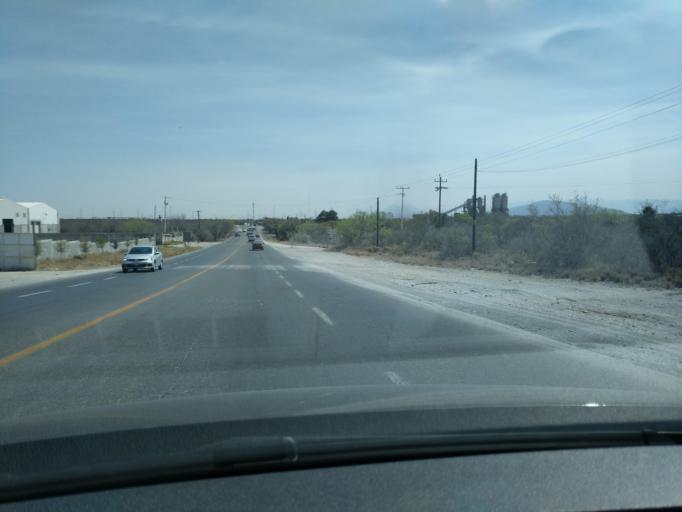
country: MX
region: Nuevo Leon
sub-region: Salinas Victoria
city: Las Torres
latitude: 25.9209
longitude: -100.3692
